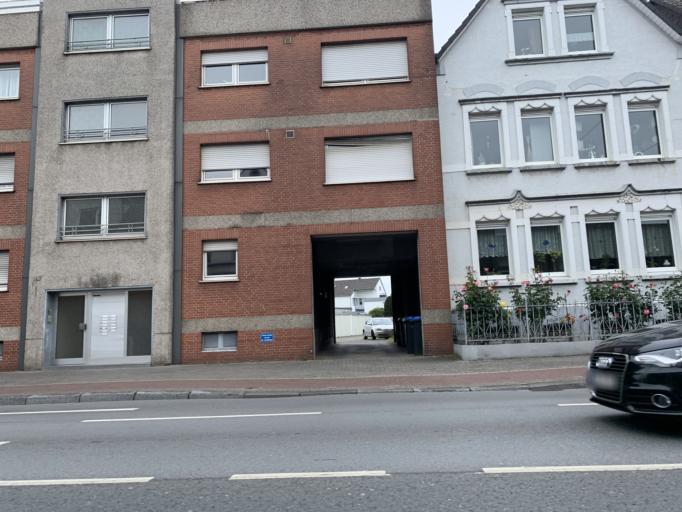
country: DE
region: North Rhine-Westphalia
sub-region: Regierungsbezirk Arnsberg
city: Hamm
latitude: 51.6653
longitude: 7.8329
